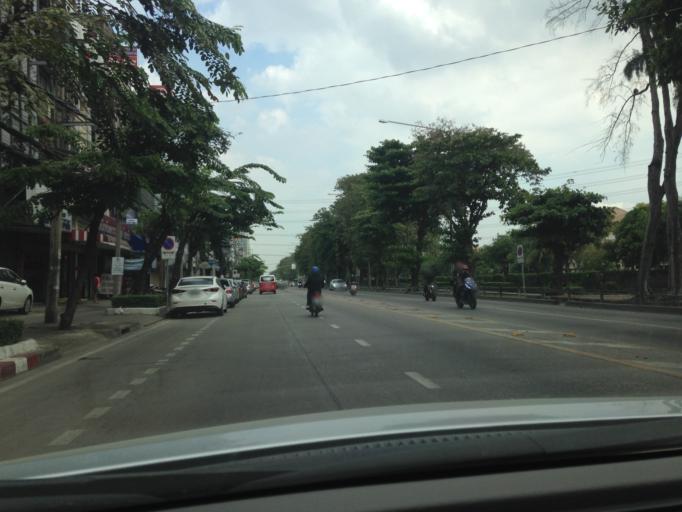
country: TH
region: Bangkok
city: Chatuchak
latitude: 13.8361
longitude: 100.5403
